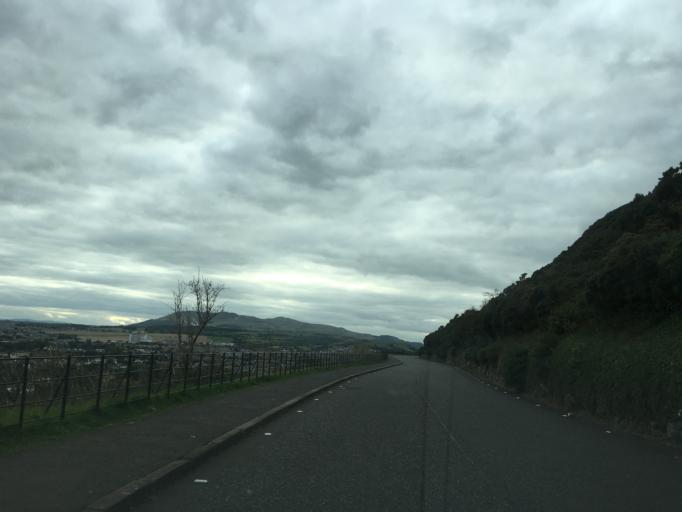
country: GB
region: Scotland
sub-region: West Lothian
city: Seafield
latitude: 55.9426
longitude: -3.1537
